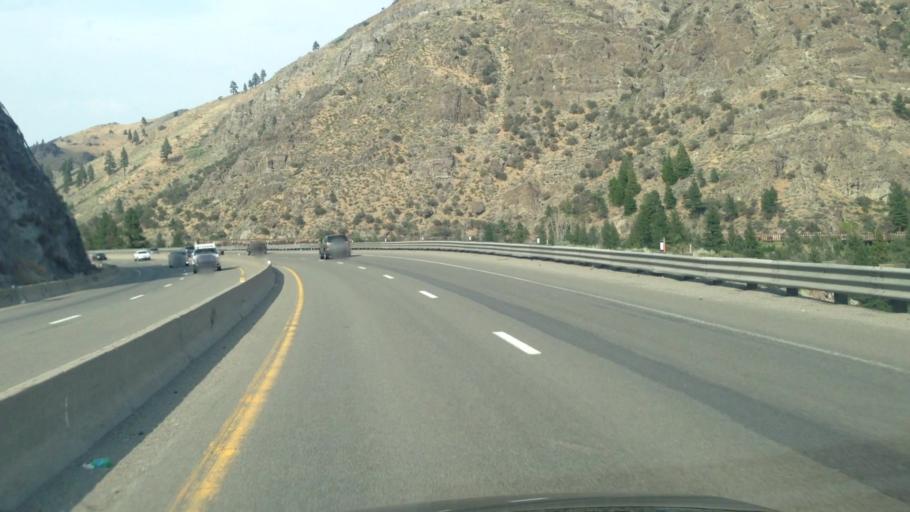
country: US
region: Nevada
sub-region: Washoe County
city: Verdi
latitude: 39.4724
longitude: -119.9975
